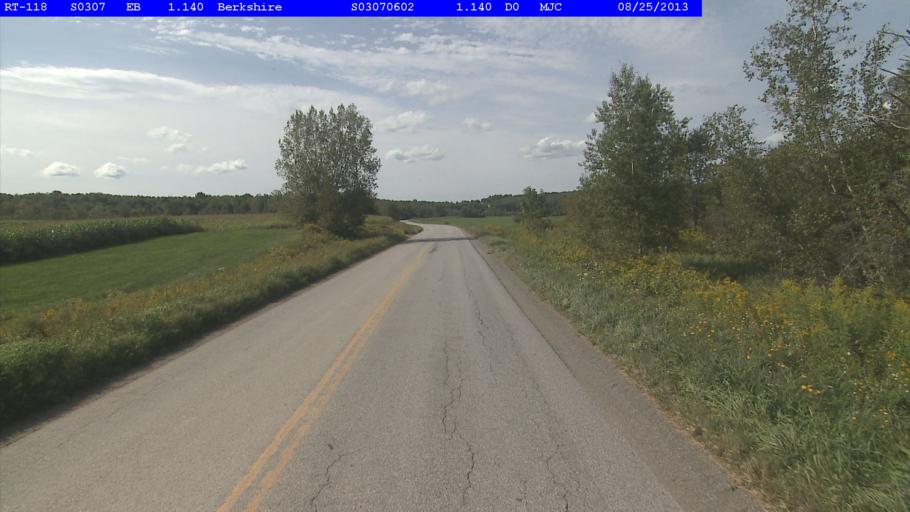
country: US
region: Vermont
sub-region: Franklin County
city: Enosburg Falls
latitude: 44.9383
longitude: -72.7329
